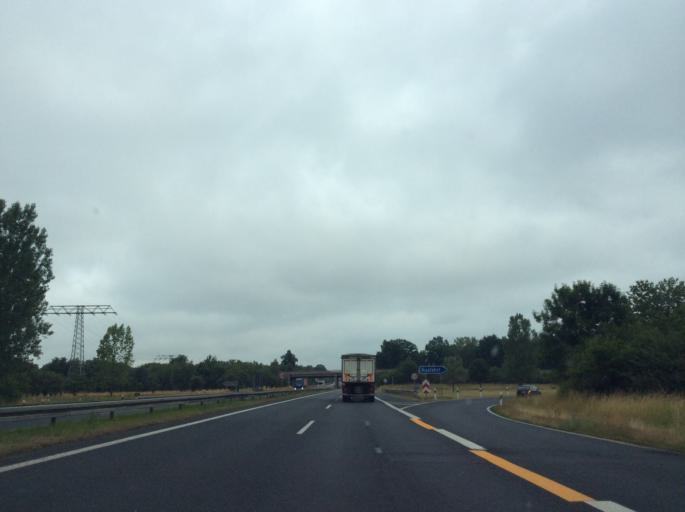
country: DE
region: Saxony
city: Radeburg
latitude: 51.2103
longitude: 13.7370
